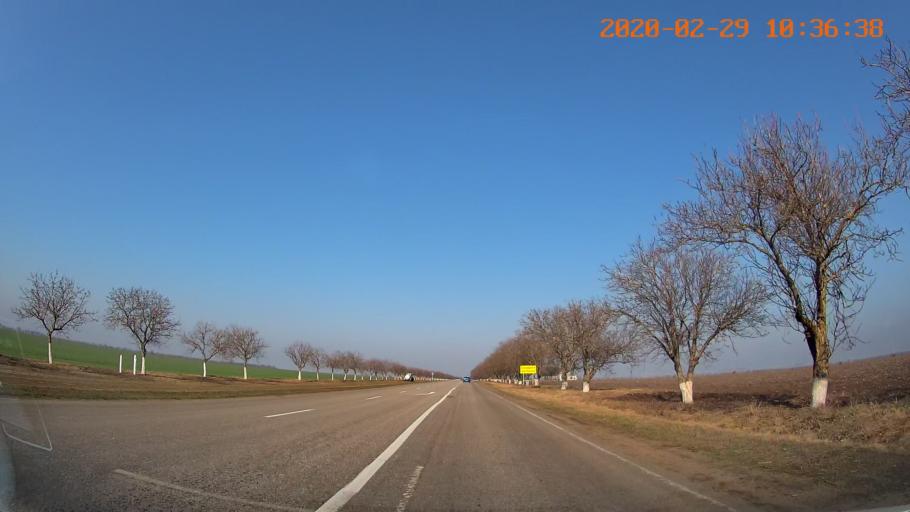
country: MD
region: Anenii Noi
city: Varnita
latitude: 46.9977
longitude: 29.5020
